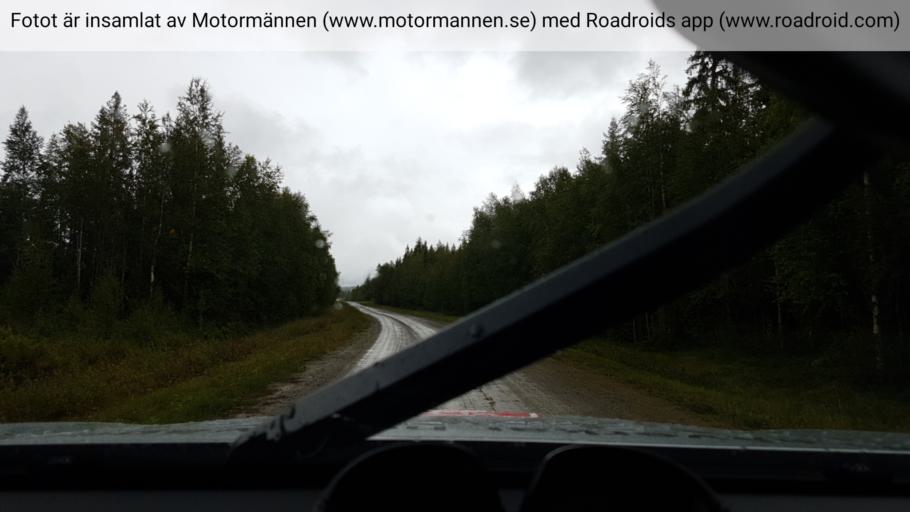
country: SE
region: Vaesterbotten
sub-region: Asele Kommun
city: Insjon
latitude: 64.7847
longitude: 17.5488
